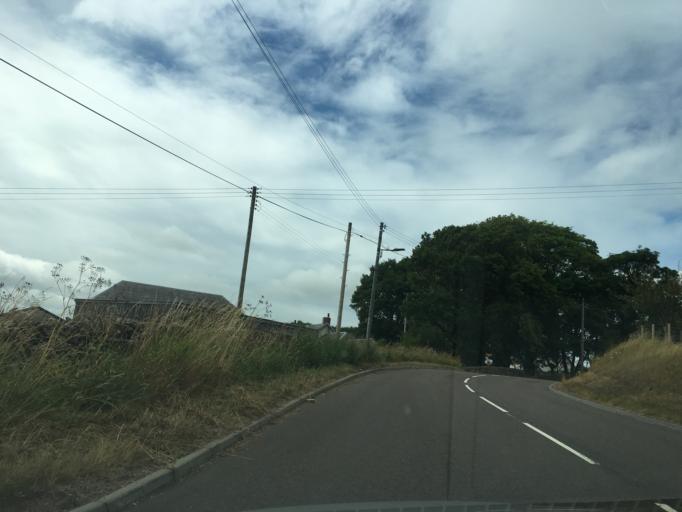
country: GB
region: Scotland
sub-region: South Lanarkshire
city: Douglas
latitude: 55.4953
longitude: -3.7753
